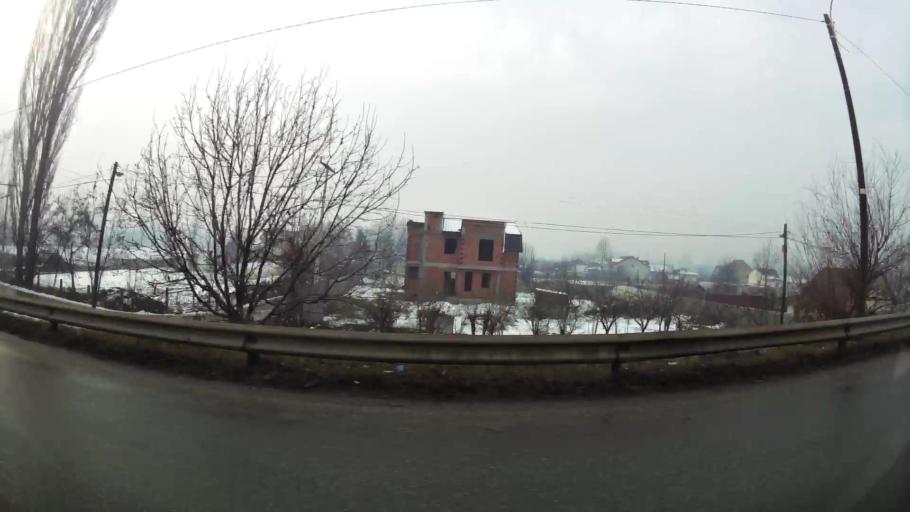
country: MK
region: Ilinden
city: Jurumleri
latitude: 41.9692
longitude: 21.5466
